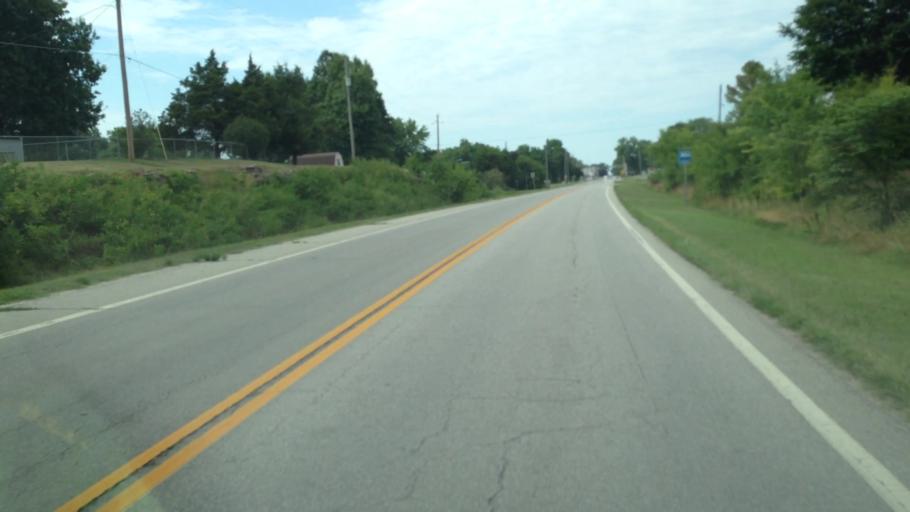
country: US
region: Kansas
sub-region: Labette County
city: Oswego
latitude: 37.1577
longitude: -95.1088
